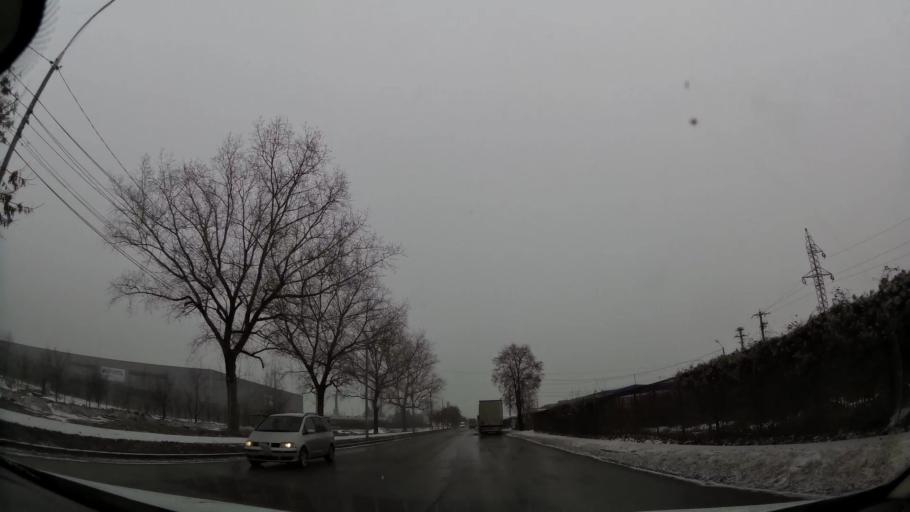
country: RO
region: Dambovita
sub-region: Municipiul Targoviste
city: Targoviste
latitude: 44.9194
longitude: 25.4363
